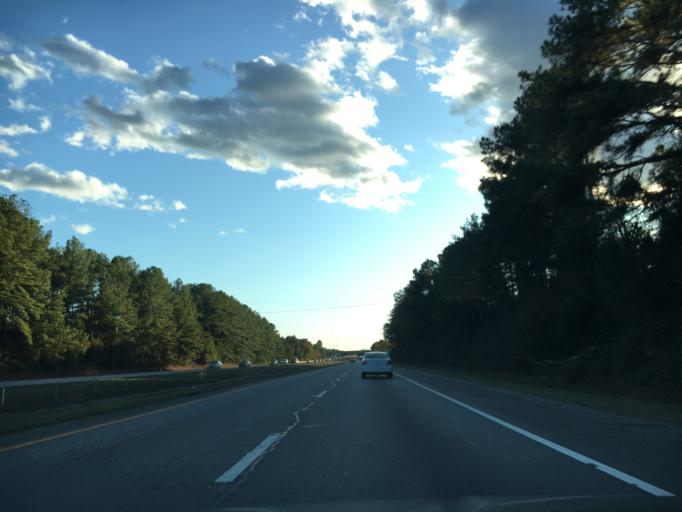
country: US
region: South Carolina
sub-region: Richland County
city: Dentsville
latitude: 34.0819
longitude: -80.9641
